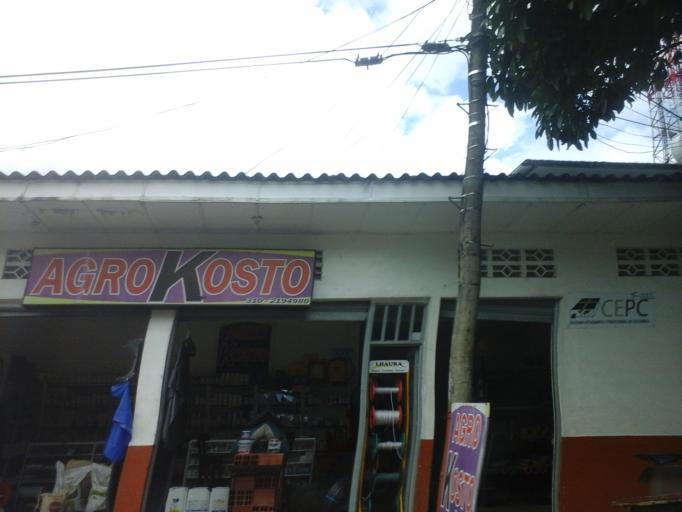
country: CO
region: Caqueta
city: El Paujil
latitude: 1.5715
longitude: -75.3258
